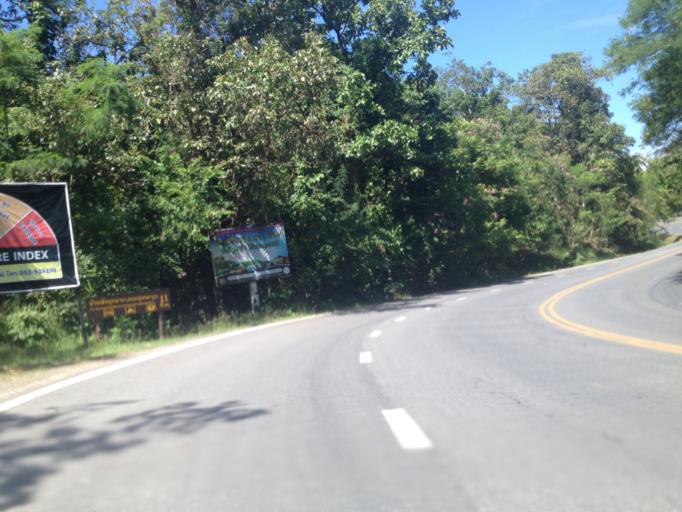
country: TH
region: Chiang Mai
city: Chiang Mai
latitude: 18.8166
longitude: 98.9451
